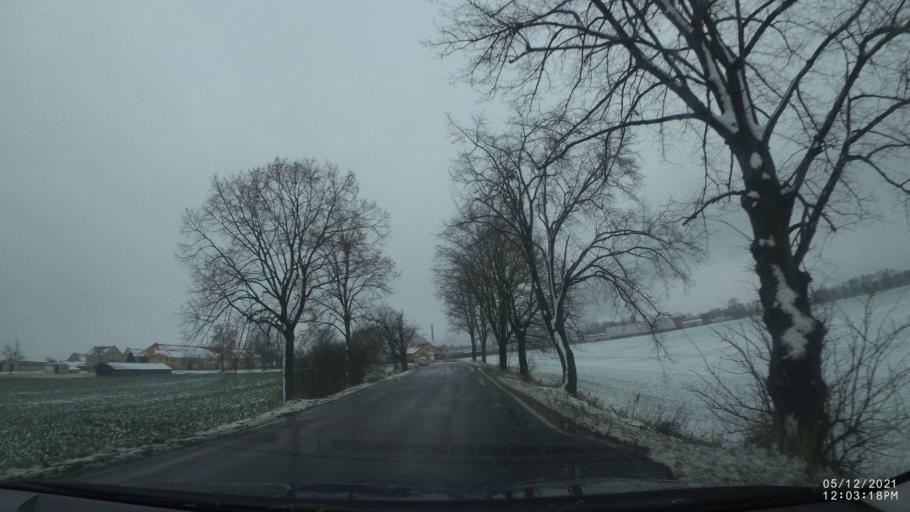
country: CZ
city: Ceske Mezirici
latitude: 50.2827
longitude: 16.0620
